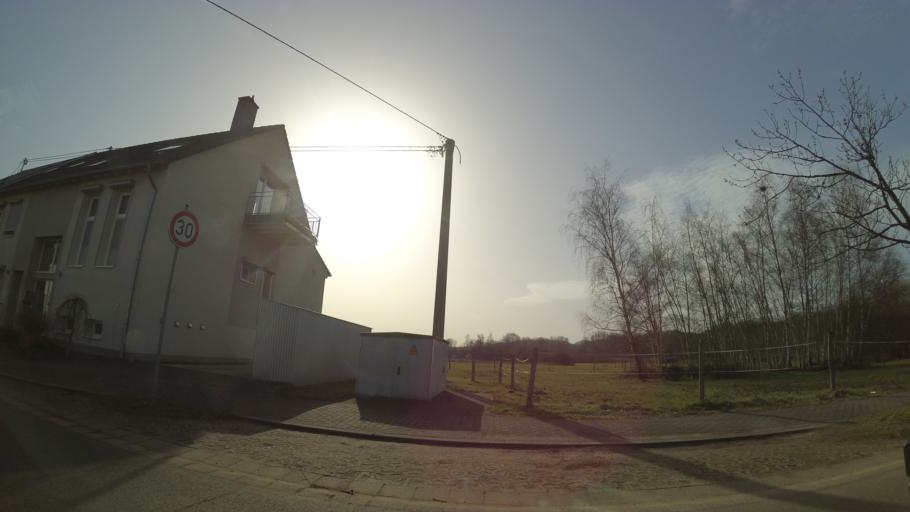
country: DE
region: Saarland
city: Saarlouis
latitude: 49.3022
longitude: 6.7548
